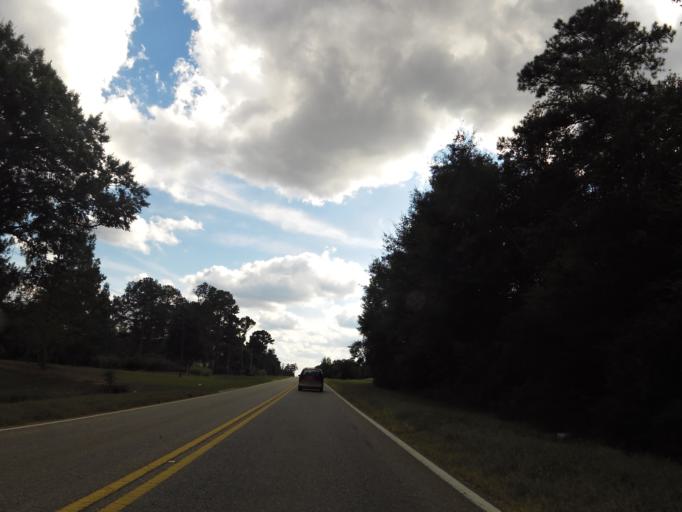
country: US
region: Alabama
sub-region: Dallas County
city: Selmont-West Selmont
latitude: 32.2828
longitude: -86.9875
